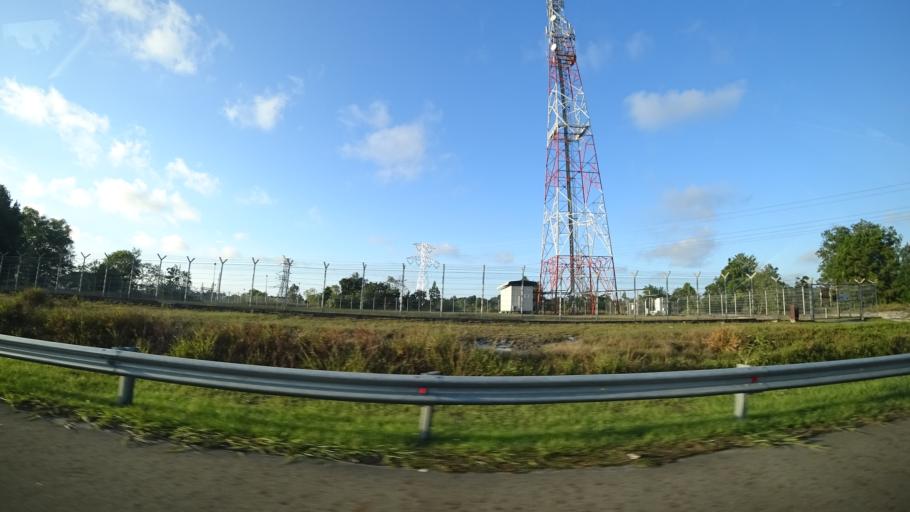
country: BN
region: Tutong
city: Tutong
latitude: 4.7445
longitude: 114.6028
